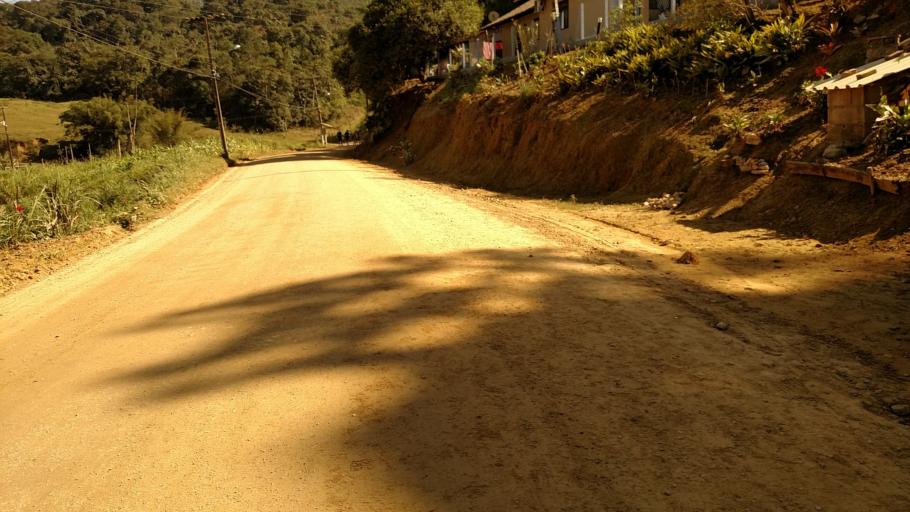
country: BR
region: Santa Catarina
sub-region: Pomerode
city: Pomerode
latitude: -26.7368
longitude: -49.0922
